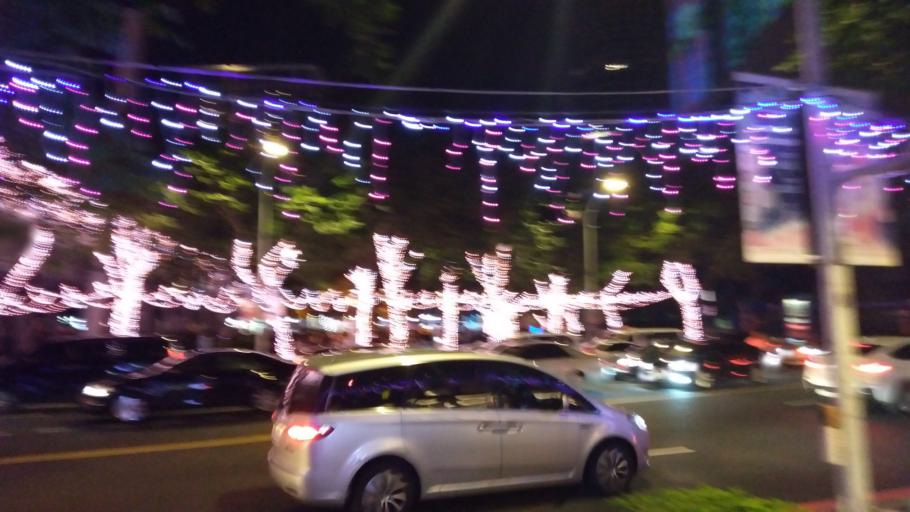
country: TW
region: Taipei
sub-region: Taipei
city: Banqiao
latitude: 25.0125
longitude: 121.4640
